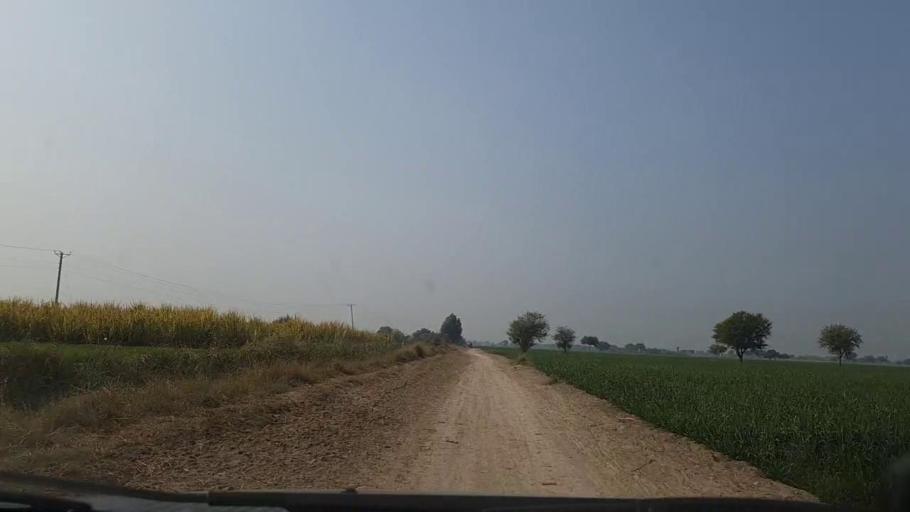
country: PK
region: Sindh
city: Sanghar
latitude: 26.0345
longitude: 68.9933
